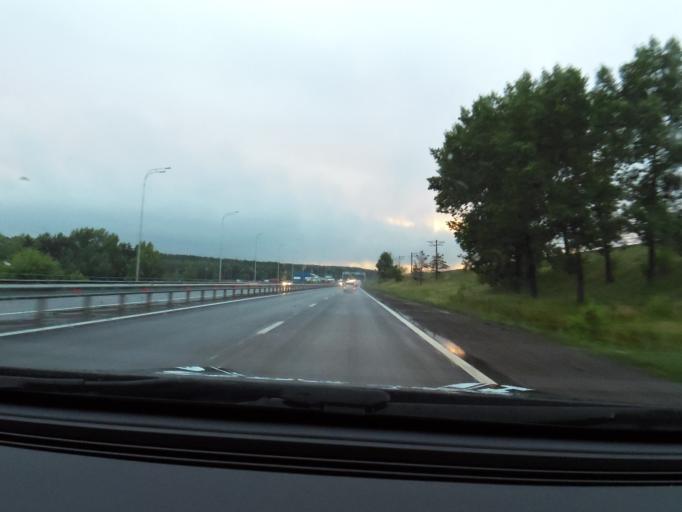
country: RU
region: Tatarstan
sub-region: Tukayevskiy Rayon
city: Naberezhnyye Chelny
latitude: 55.7160
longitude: 52.2671
